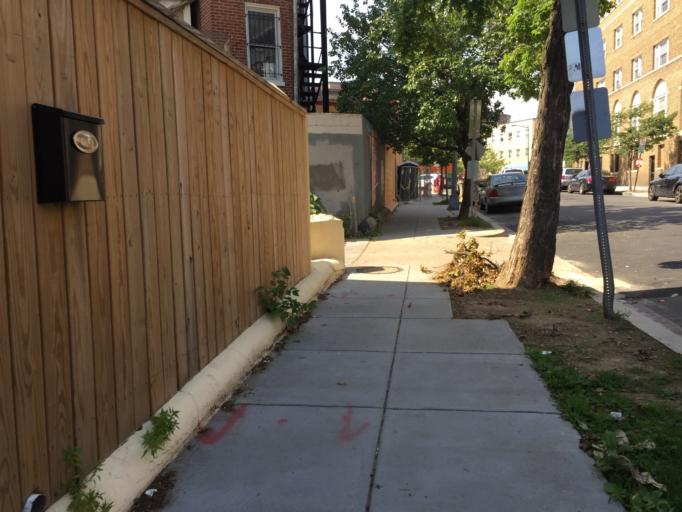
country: US
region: Washington, D.C.
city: Washington, D.C.
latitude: 38.9236
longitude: -77.0403
